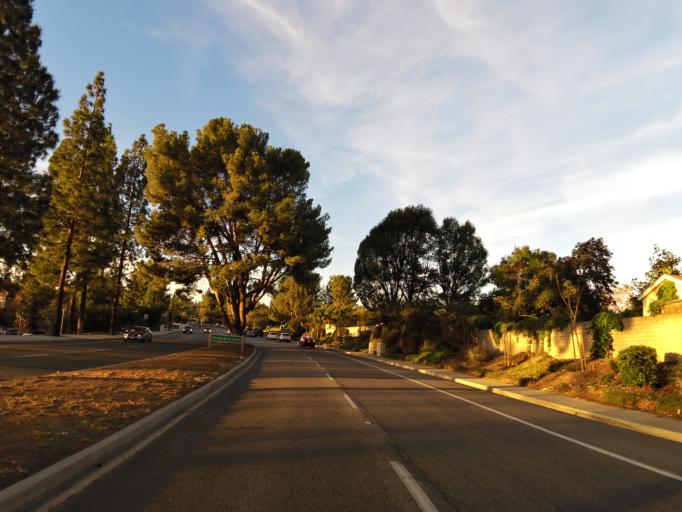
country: US
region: California
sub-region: Ventura County
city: Thousand Oaks
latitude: 34.2104
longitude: -118.8396
